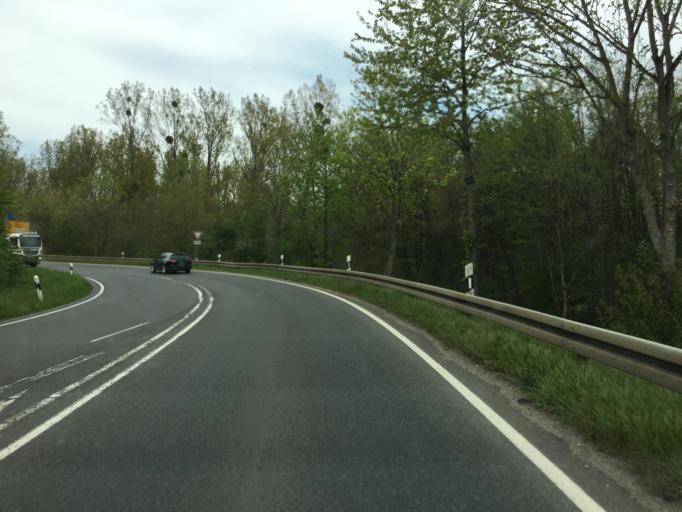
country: DE
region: North Rhine-Westphalia
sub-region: Regierungsbezirk Koln
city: Erftstadt
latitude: 50.8223
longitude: 6.8177
